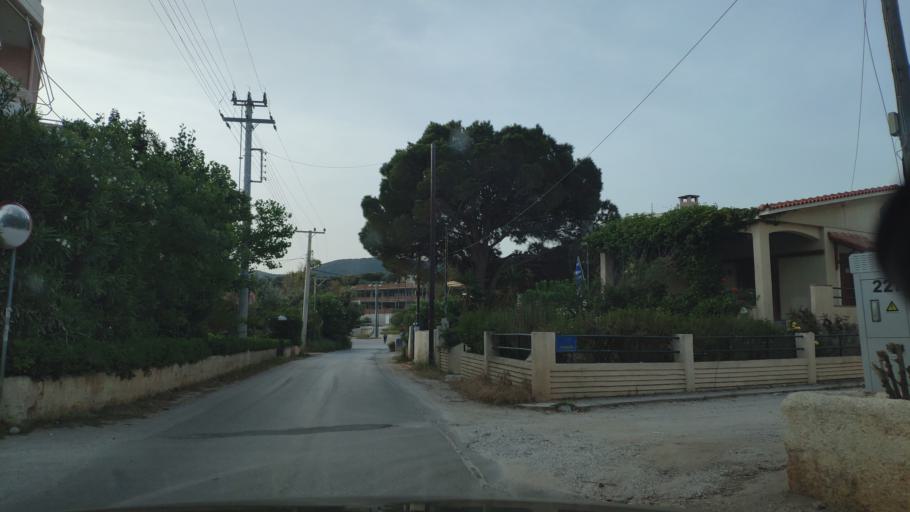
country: GR
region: Attica
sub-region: Nomarchia Anatolikis Attikis
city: Limin Mesoyaias
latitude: 37.8682
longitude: 24.0315
